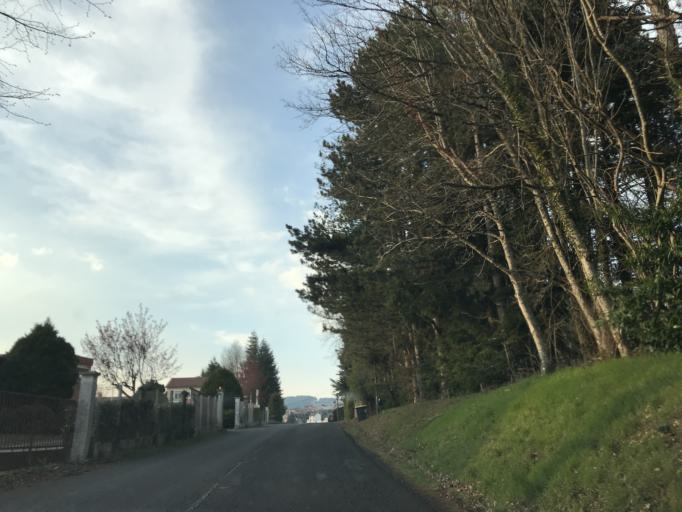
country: FR
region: Auvergne
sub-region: Departement du Puy-de-Dome
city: Saint-Remy-sur-Durolle
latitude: 45.8794
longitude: 3.5929
